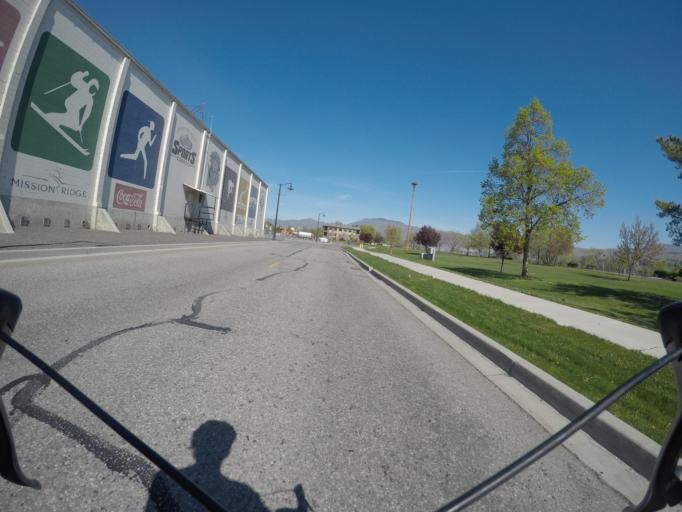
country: US
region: Washington
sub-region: Chelan County
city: Wenatchee
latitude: 47.4303
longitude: -120.3109
